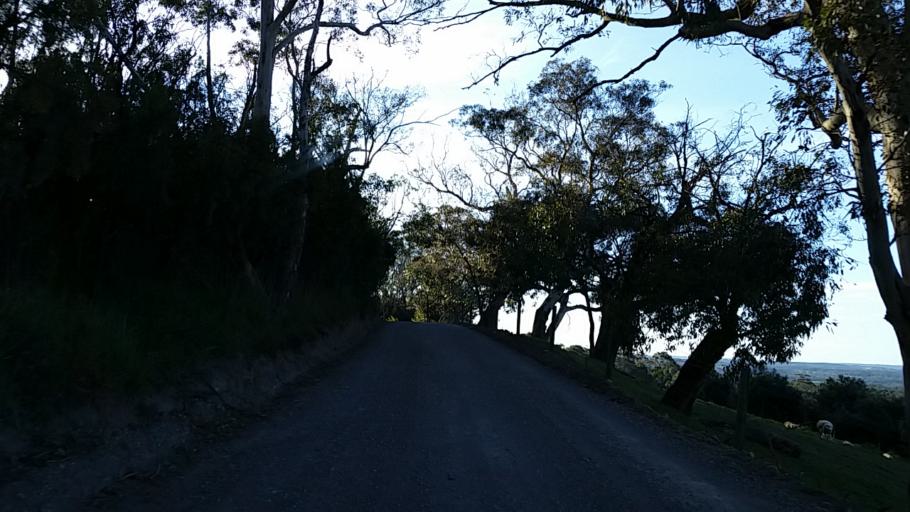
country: AU
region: South Australia
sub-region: Mount Barker
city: Meadows
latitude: -35.2289
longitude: 138.7384
